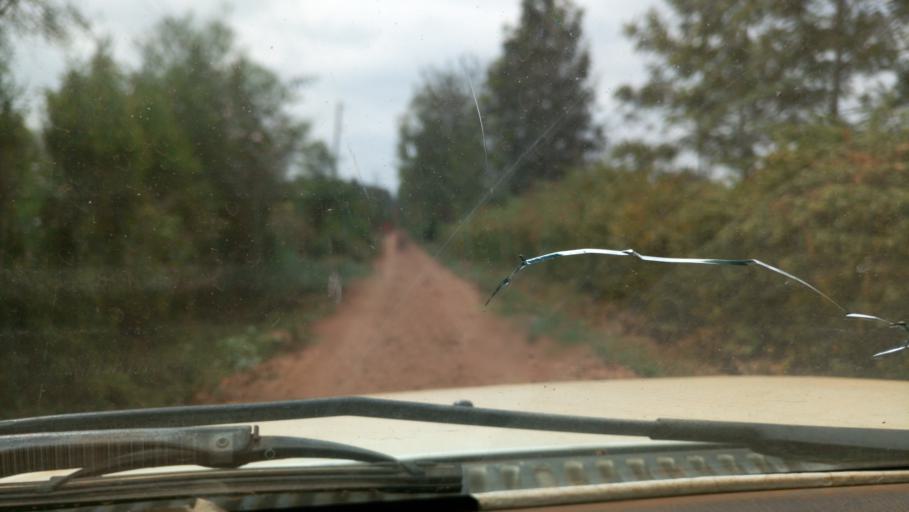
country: KE
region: Murang'a District
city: Maragua
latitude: -0.8992
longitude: 37.1961
